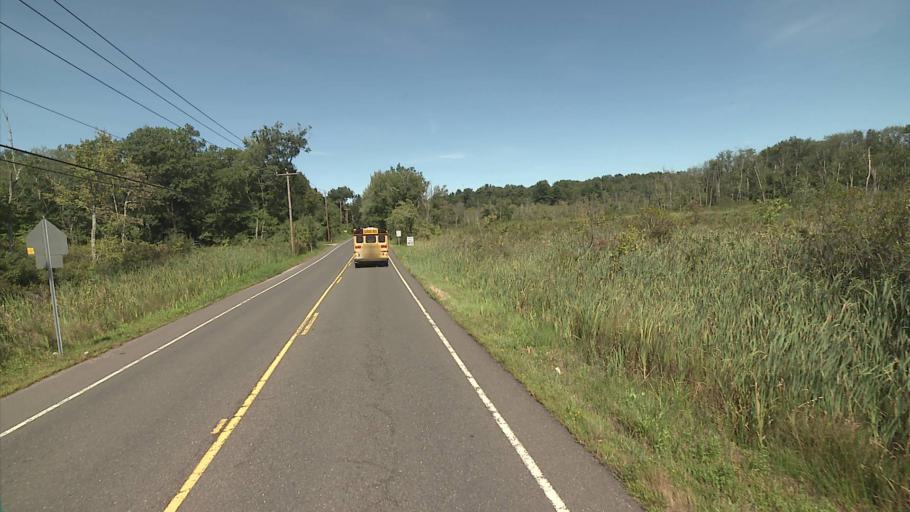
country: US
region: Connecticut
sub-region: New Haven County
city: Middlebury
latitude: 41.5045
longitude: -73.1502
